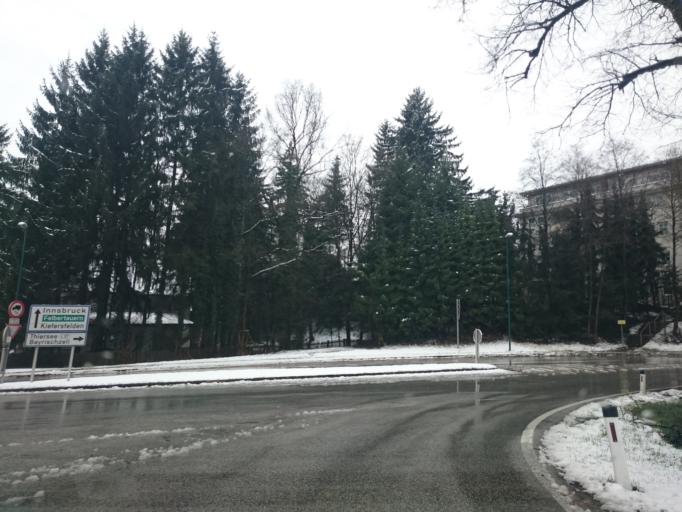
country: AT
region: Tyrol
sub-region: Politischer Bezirk Kufstein
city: Kufstein
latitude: 47.5885
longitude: 12.1620
